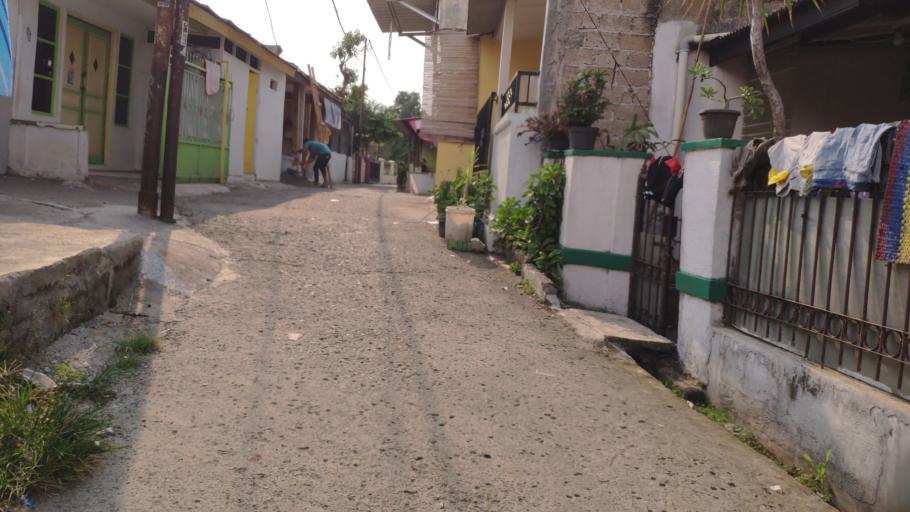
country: ID
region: West Java
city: Pamulang
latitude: -6.3293
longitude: 106.7947
